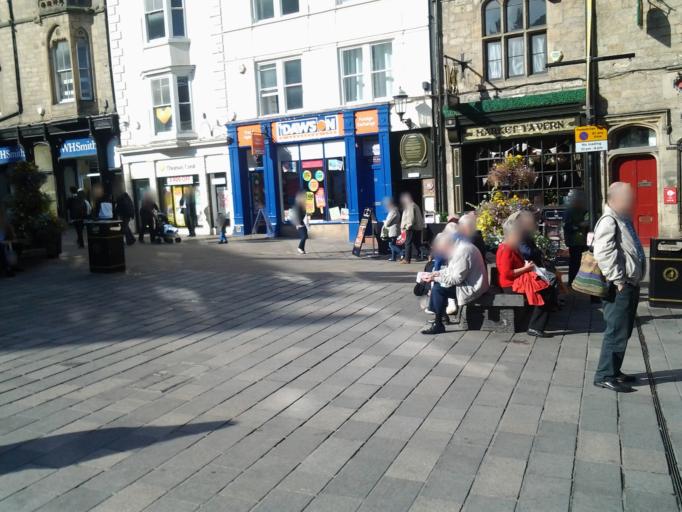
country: GB
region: England
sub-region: County Durham
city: Durham
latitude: 54.7771
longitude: -1.5755
